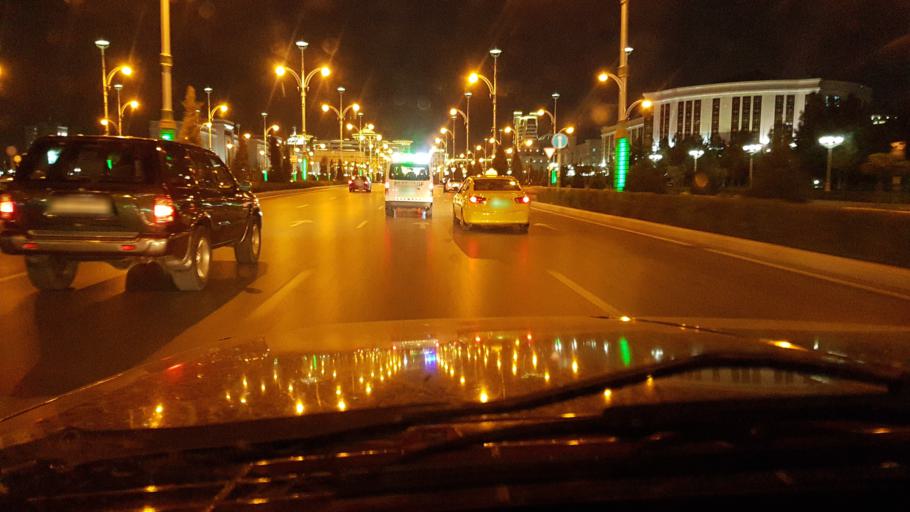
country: TM
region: Ahal
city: Ashgabat
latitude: 37.8984
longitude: 58.3613
